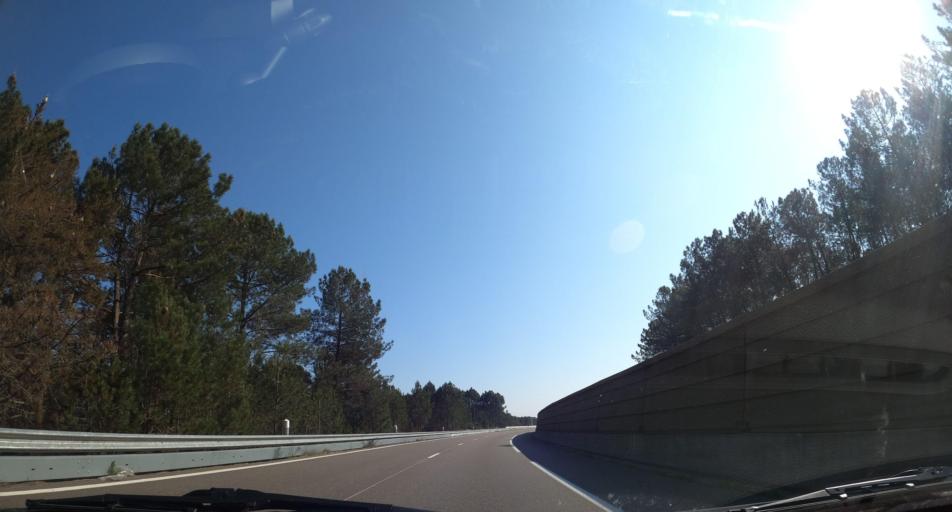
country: FR
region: Aquitaine
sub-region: Departement des Landes
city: Saint-Geours-de-Maremne
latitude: 43.6968
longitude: -1.2274
